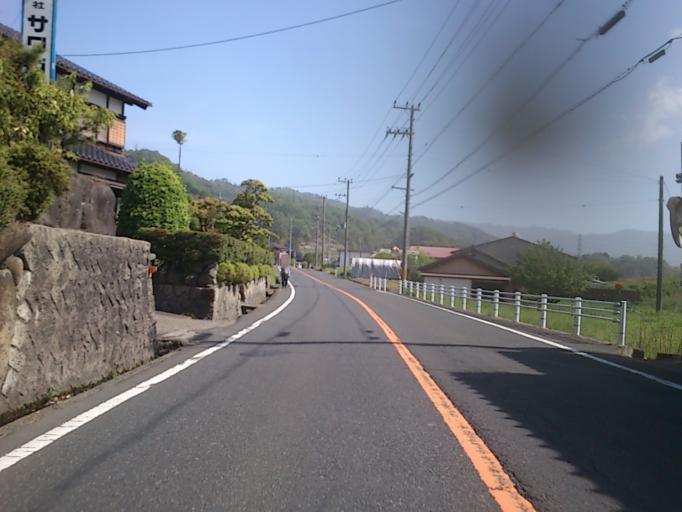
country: JP
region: Kyoto
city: Miyazu
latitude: 35.5553
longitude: 135.1390
